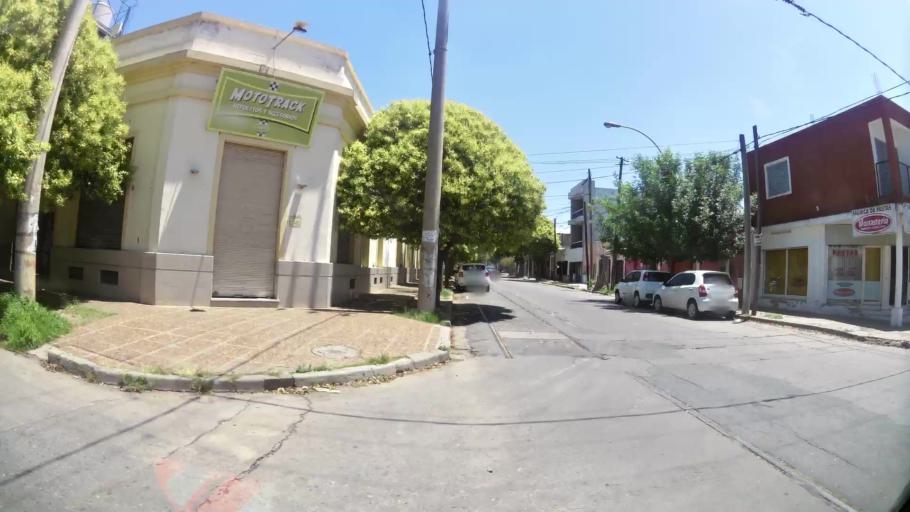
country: AR
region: Cordoba
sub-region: Departamento de Capital
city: Cordoba
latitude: -31.4060
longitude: -64.2196
